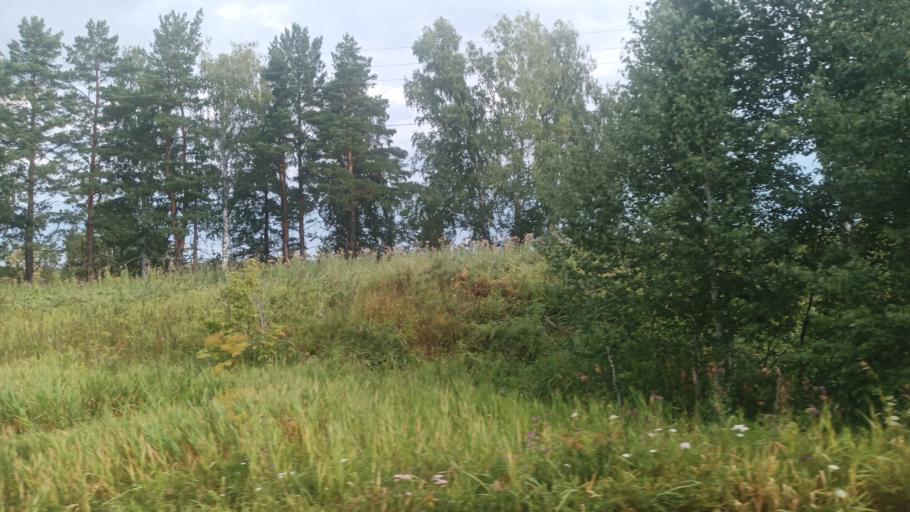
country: RU
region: Altai Krai
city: Nalobikha
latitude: 53.2364
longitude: 84.4716
